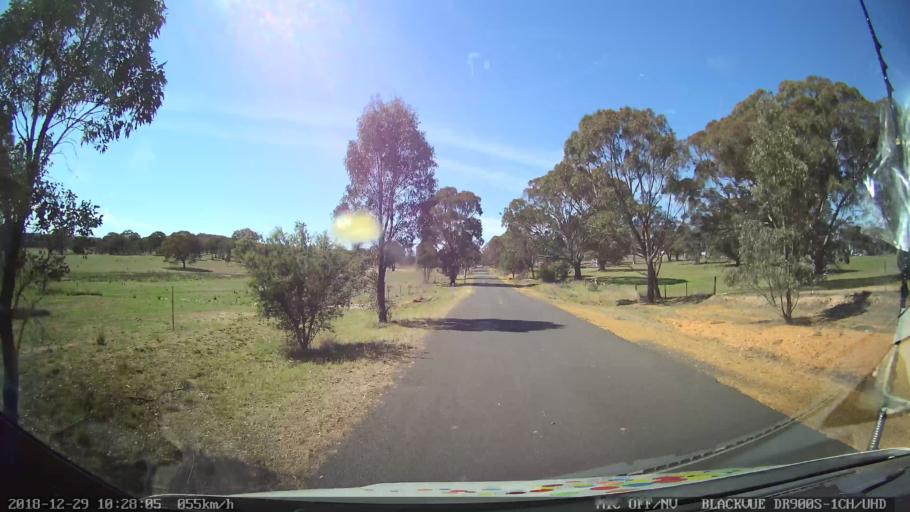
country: AU
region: New South Wales
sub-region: Yass Valley
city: Gundaroo
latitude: -34.9397
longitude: 149.4537
